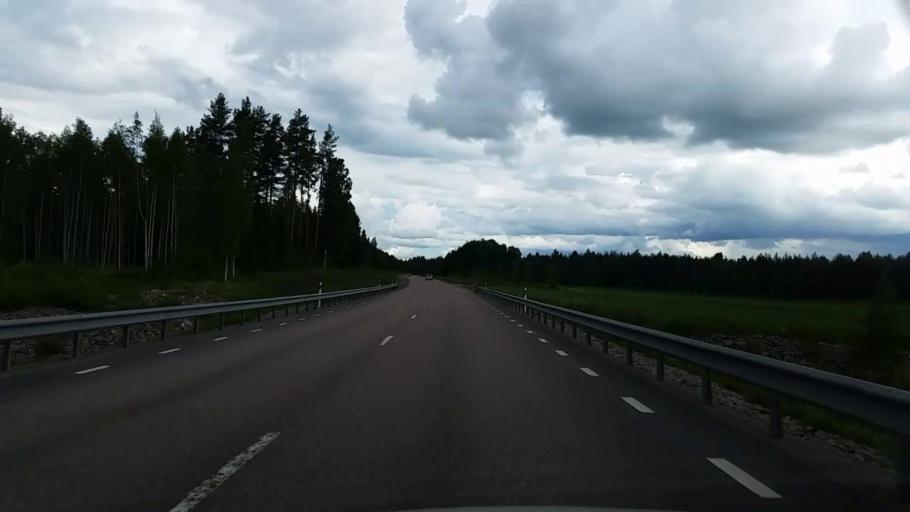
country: SE
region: Gaevleborg
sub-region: Hofors Kommun
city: Hofors
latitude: 60.4746
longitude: 16.4476
